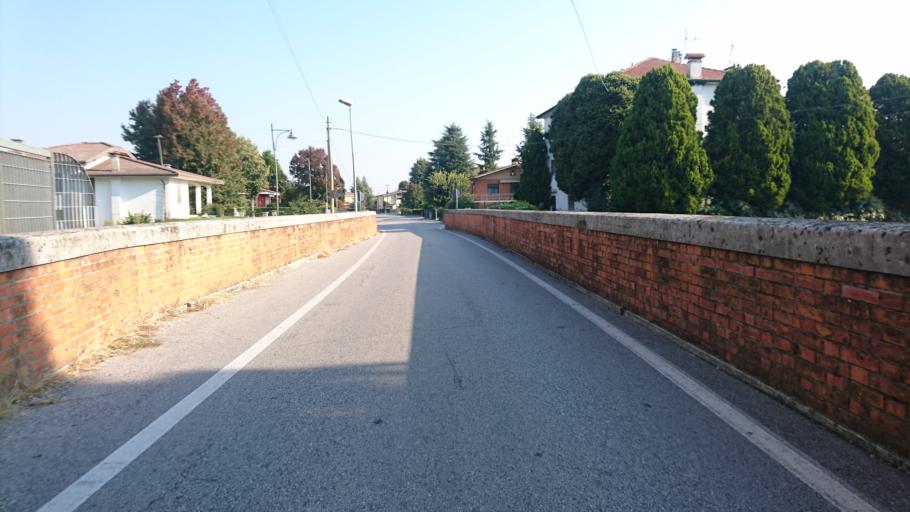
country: IT
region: Veneto
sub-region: Provincia di Padova
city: Grantorto
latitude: 45.6003
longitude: 11.7307
